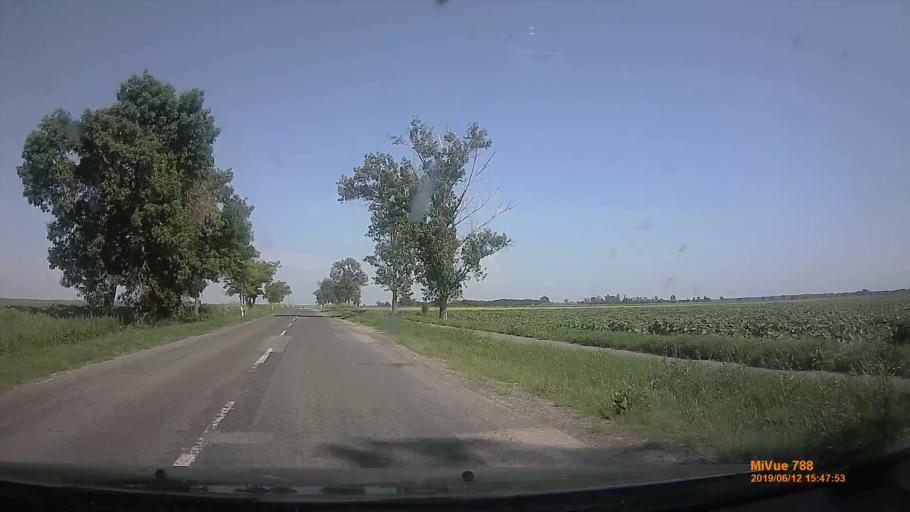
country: HU
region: Csongrad
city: Mako
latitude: 46.2054
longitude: 20.5399
